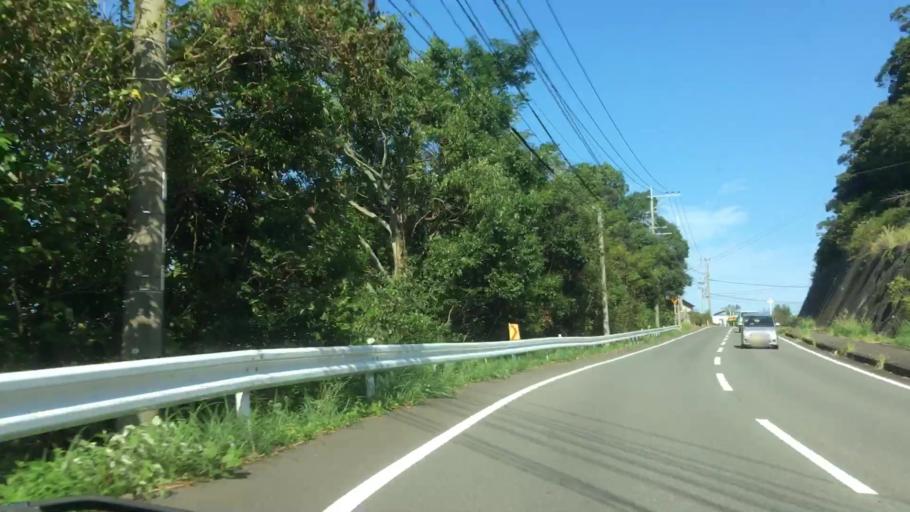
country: JP
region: Nagasaki
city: Sasebo
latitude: 33.0046
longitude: 129.6577
